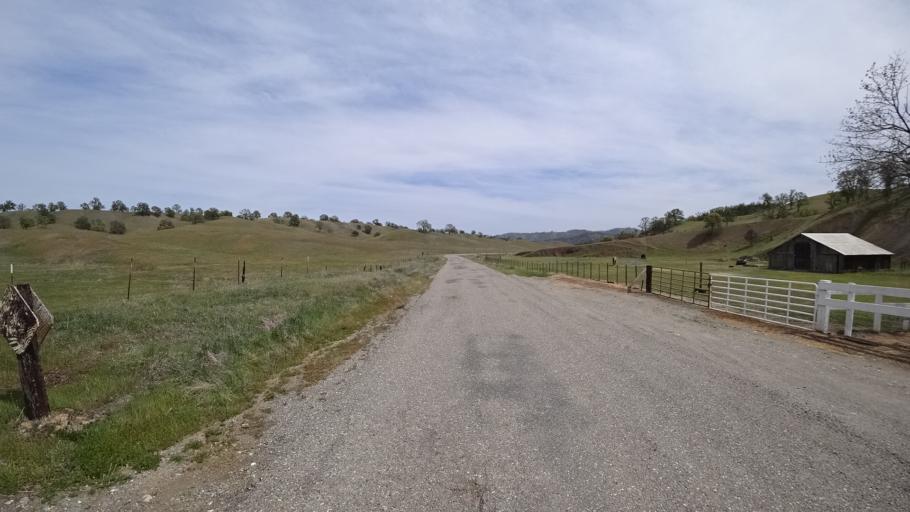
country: US
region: California
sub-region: Glenn County
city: Willows
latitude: 39.6136
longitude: -122.5708
